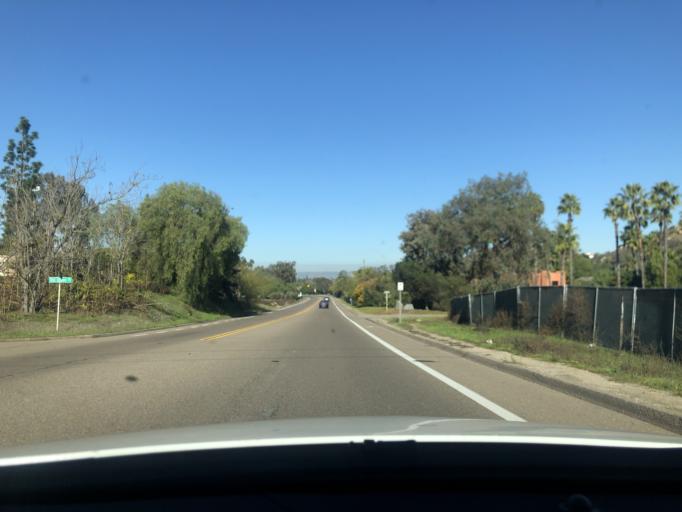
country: US
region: California
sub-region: San Diego County
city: El Cajon
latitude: 32.7761
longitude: -116.9428
